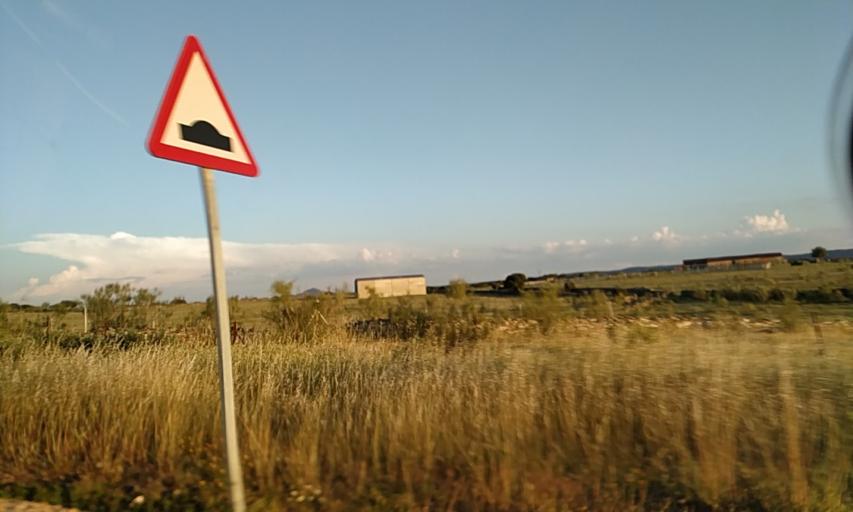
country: ES
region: Extremadura
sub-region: Provincia de Caceres
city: Salorino
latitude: 39.5145
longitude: -7.0534
